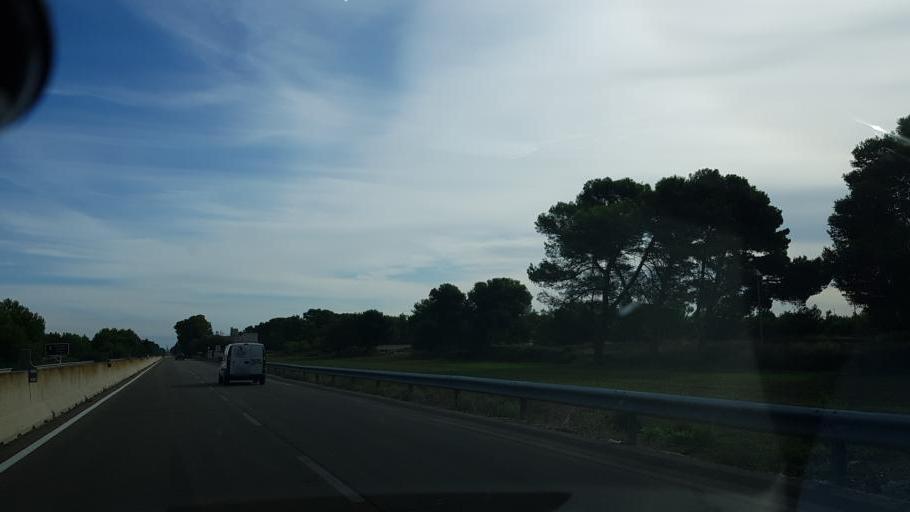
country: IT
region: Apulia
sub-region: Provincia di Lecce
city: Struda
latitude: 40.3823
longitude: 18.2771
